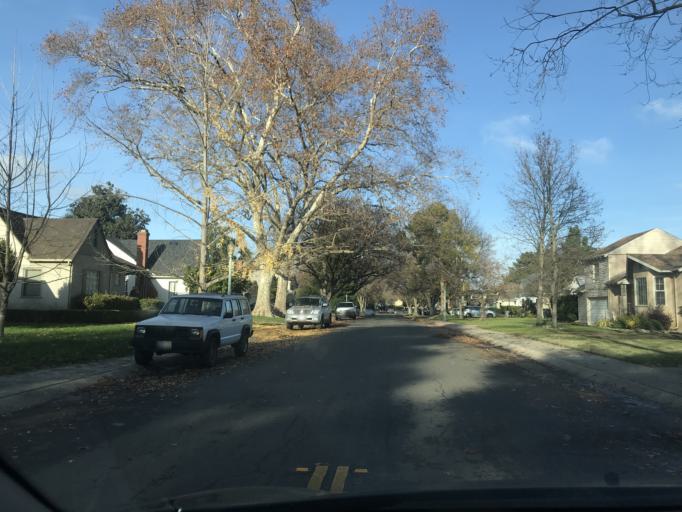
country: US
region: California
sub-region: Sacramento County
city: Sacramento
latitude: 38.5586
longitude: -121.4966
